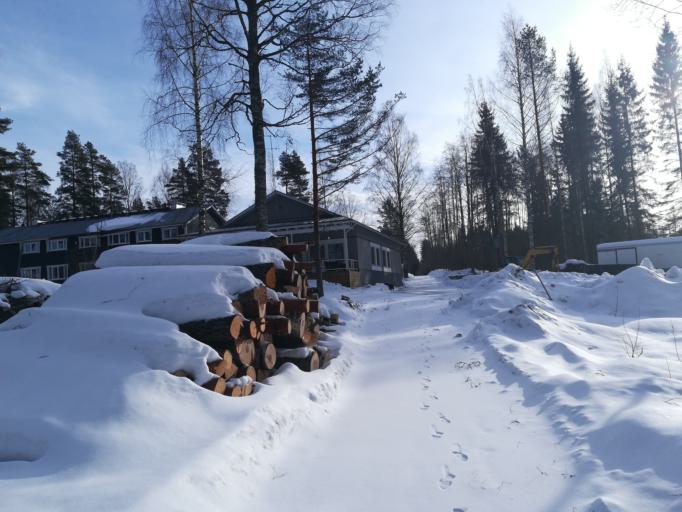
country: FI
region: Southern Savonia
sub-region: Savonlinna
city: Savonlinna
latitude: 61.8294
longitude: 29.0227
